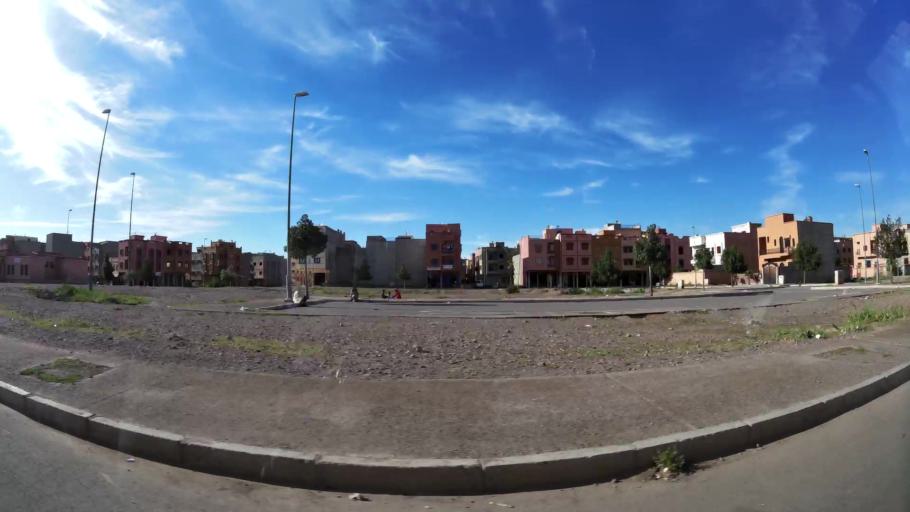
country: MA
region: Marrakech-Tensift-Al Haouz
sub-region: Marrakech
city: Marrakesh
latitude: 31.6885
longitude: -8.0656
